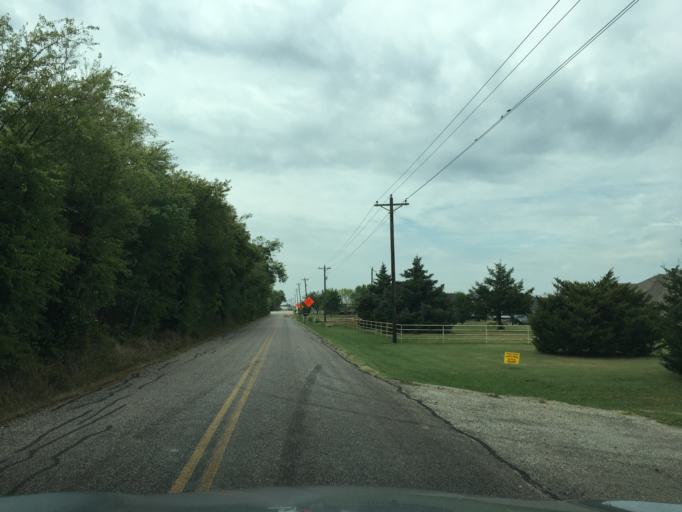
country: US
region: Texas
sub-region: Collin County
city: Anna
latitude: 33.3068
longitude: -96.5267
